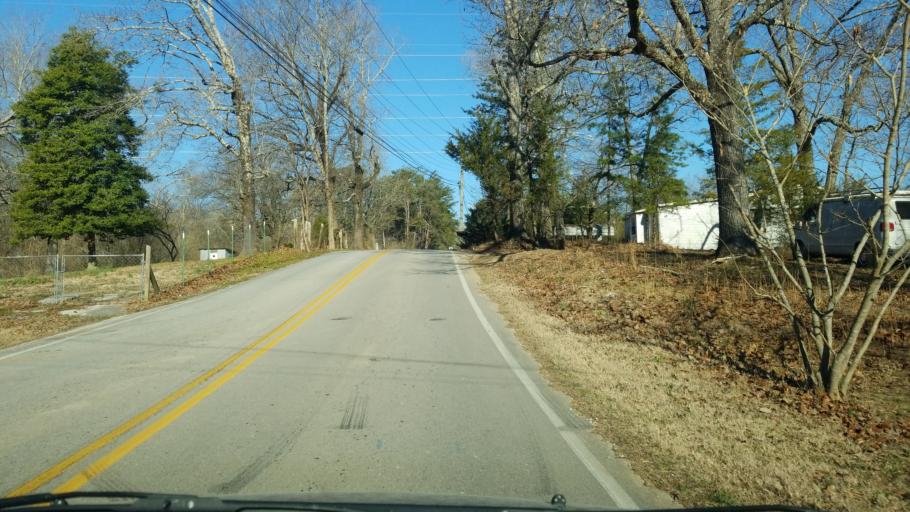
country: US
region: Tennessee
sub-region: Hamilton County
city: Collegedale
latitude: 35.0599
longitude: -85.0949
